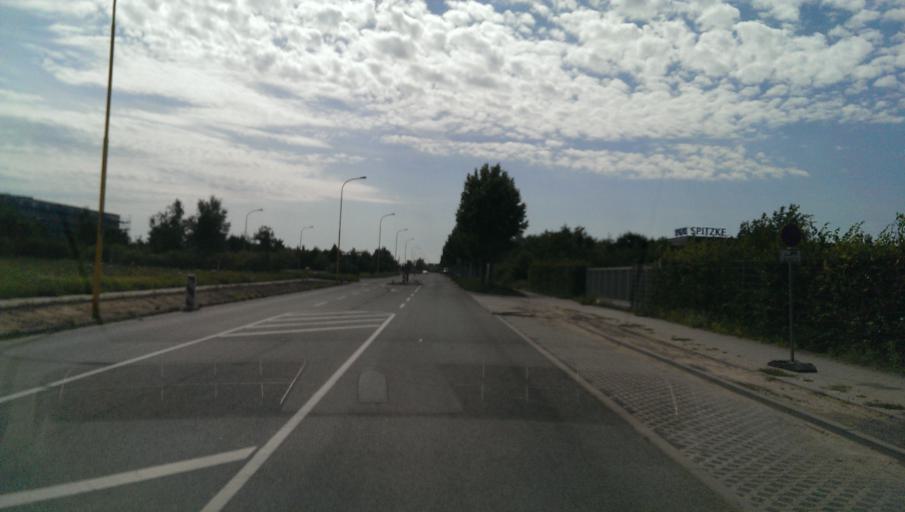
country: DE
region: Brandenburg
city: Grossbeeren
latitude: 52.3742
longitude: 13.2989
